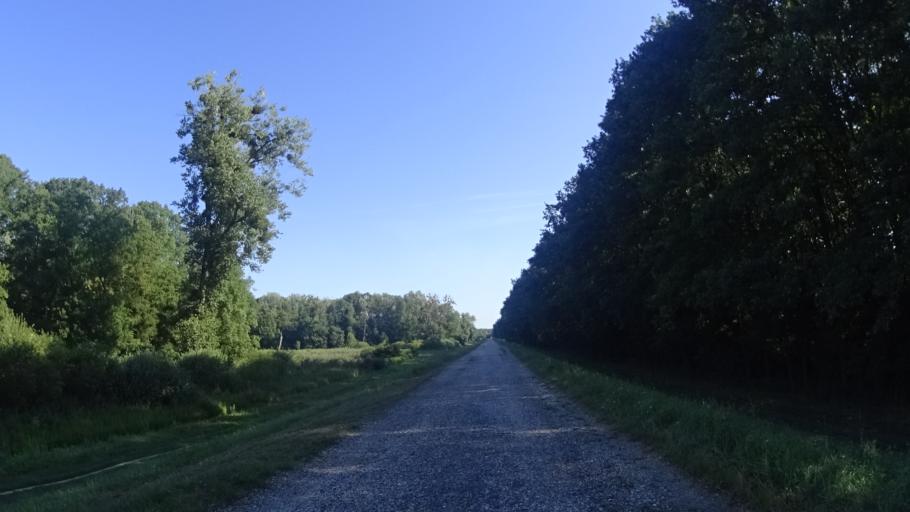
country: CZ
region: South Moravian
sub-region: Okres Breclav
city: Lanzhot
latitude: 48.6545
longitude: 16.9760
